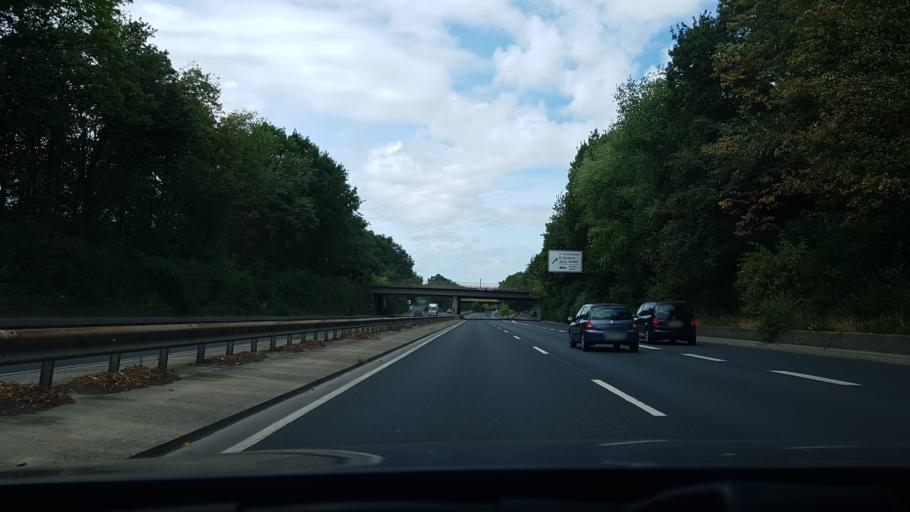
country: DE
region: North Rhine-Westphalia
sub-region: Regierungsbezirk Dusseldorf
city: Hilden
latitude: 51.1683
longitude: 6.8576
